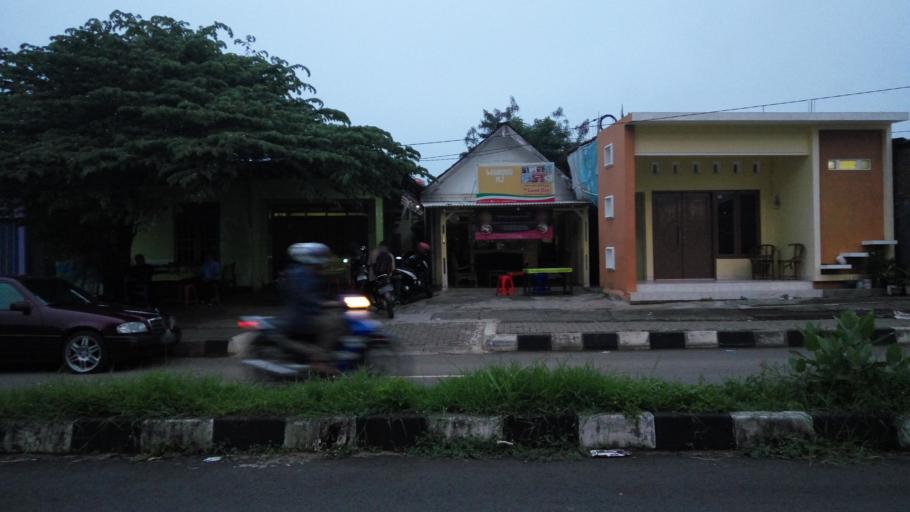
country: ID
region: Central Java
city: Semarang
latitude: -7.0521
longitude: 110.4432
